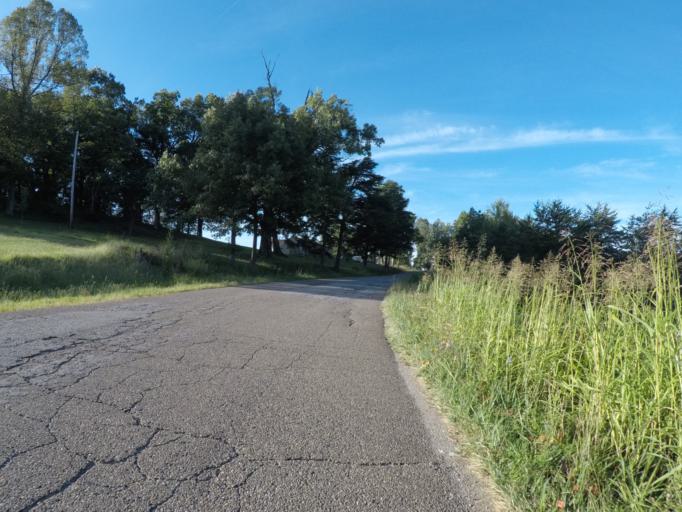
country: US
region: Ohio
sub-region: Lawrence County
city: Coal Grove
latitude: 38.5939
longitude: -82.5471
